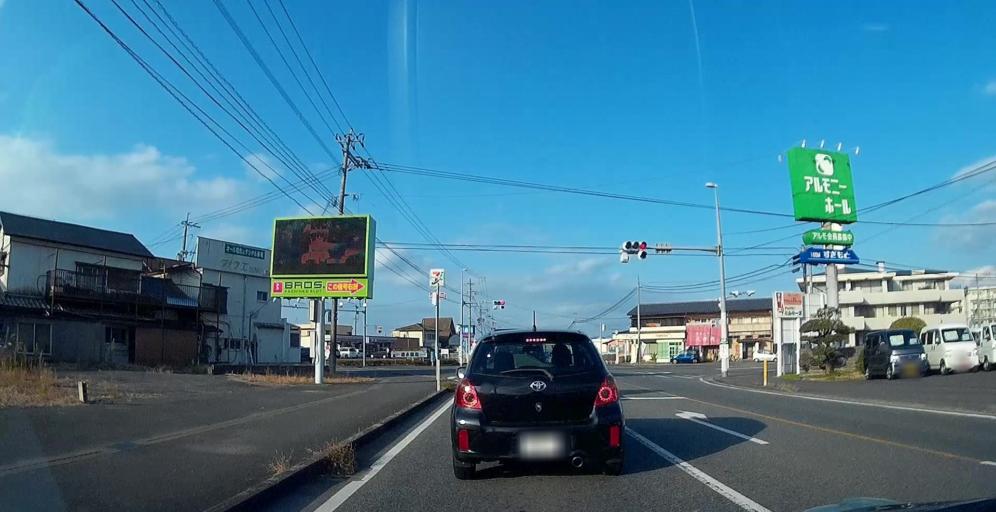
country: JP
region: Kumamoto
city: Matsubase
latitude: 32.5944
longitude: 130.7025
